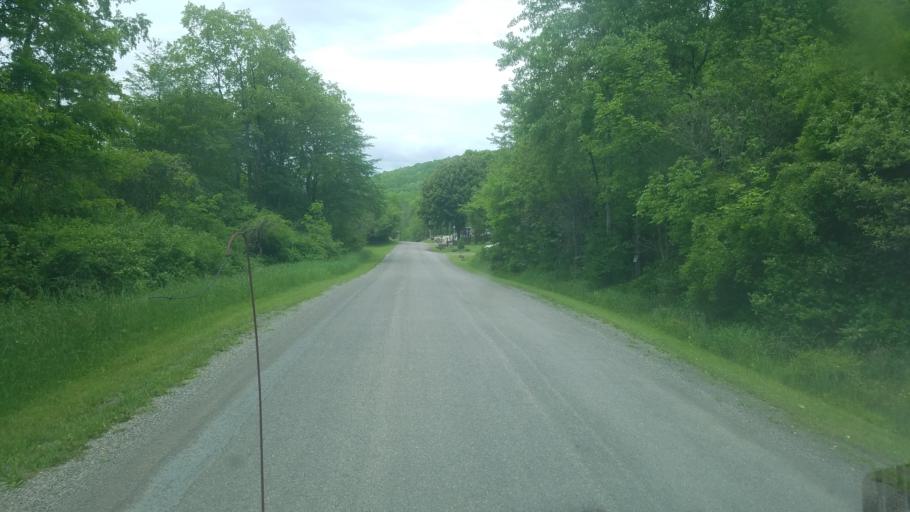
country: US
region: Pennsylvania
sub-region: Tioga County
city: Westfield
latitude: 41.8853
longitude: -77.5978
